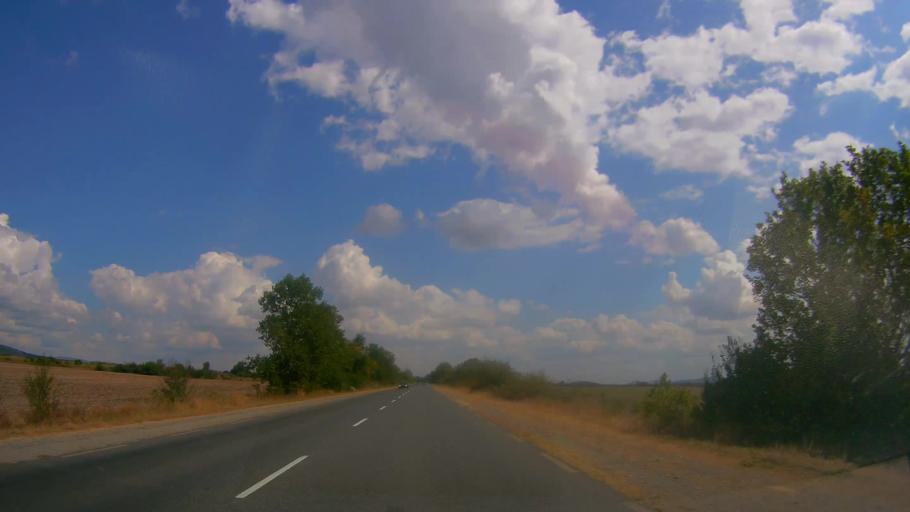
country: BG
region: Sliven
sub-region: Obshtina Sliven
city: Kermen
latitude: 42.6339
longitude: 26.1643
